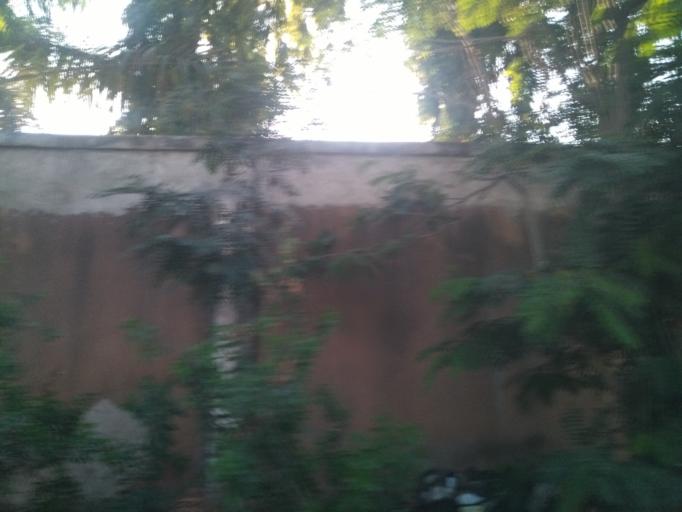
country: TZ
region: Dar es Salaam
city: Dar es Salaam
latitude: -6.9082
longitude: 39.2673
